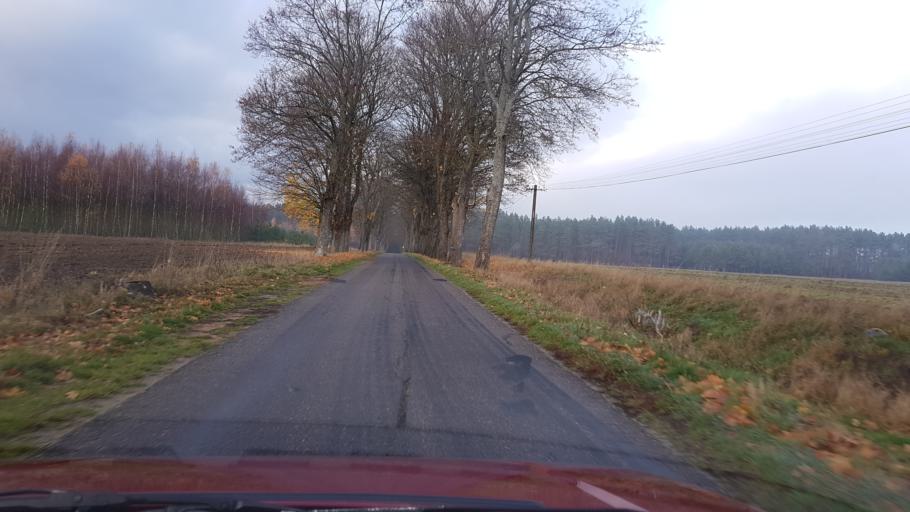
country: PL
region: West Pomeranian Voivodeship
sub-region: Powiat bialogardzki
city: Tychowo
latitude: 53.9642
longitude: 16.3170
